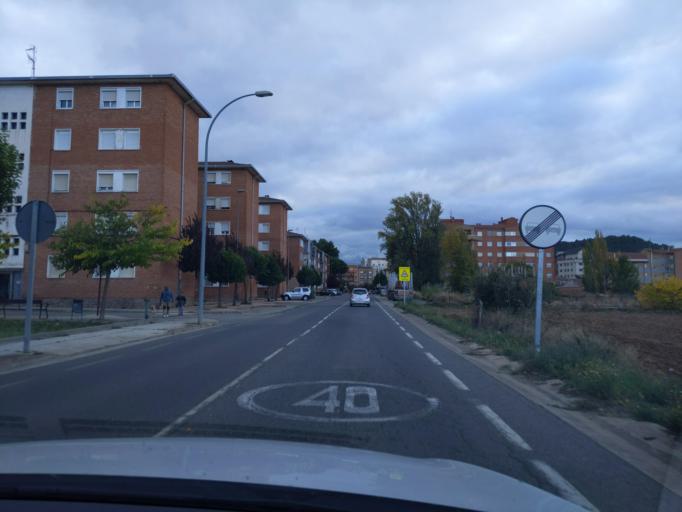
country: ES
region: La Rioja
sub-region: Provincia de La Rioja
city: Najera
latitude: 42.4208
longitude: -2.7237
